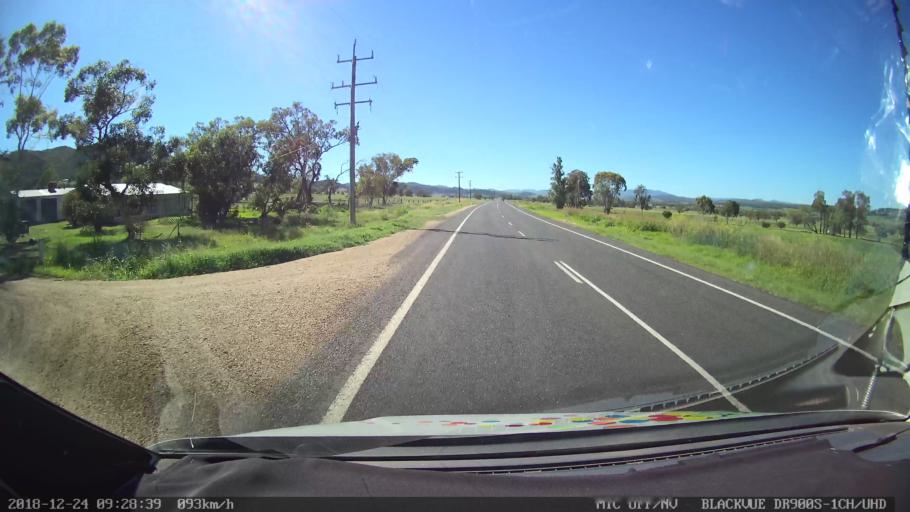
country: AU
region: New South Wales
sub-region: Liverpool Plains
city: Quirindi
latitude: -31.5401
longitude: 150.6905
